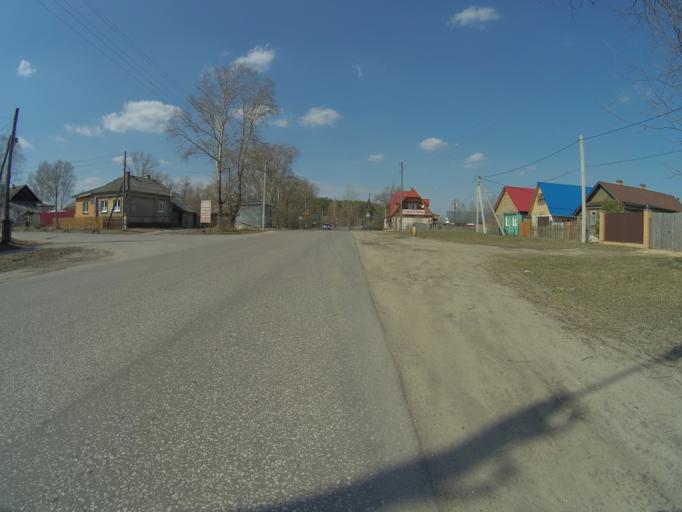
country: RU
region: Vladimir
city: Sudogda
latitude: 55.9578
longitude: 40.8622
